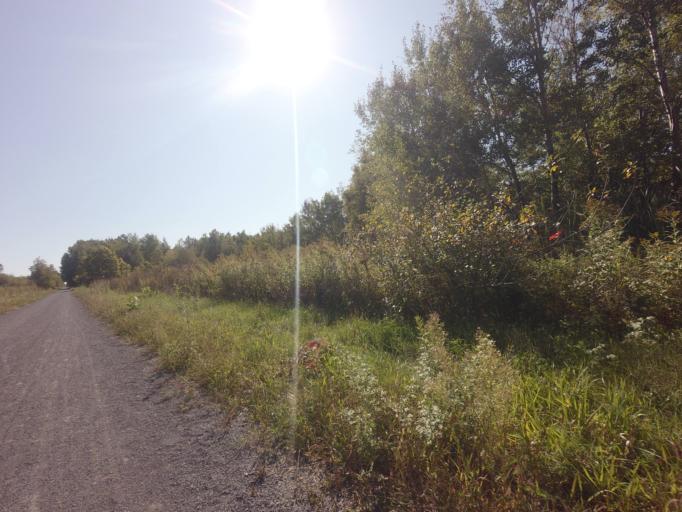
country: CA
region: Ontario
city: Ottawa
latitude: 45.4194
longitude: -75.4793
